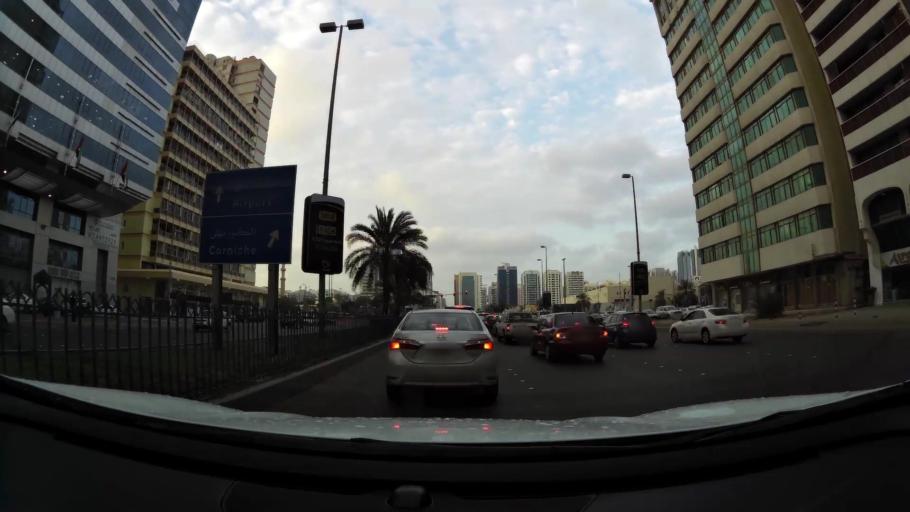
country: AE
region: Abu Dhabi
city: Abu Dhabi
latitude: 24.4838
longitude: 54.3603
